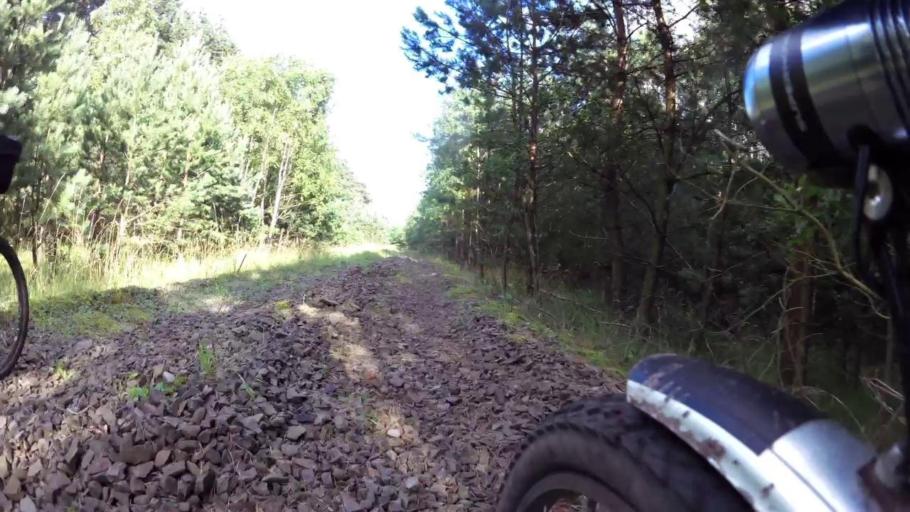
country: PL
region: West Pomeranian Voivodeship
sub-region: Powiat swidwinski
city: Swidwin
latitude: 53.7634
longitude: 15.8868
